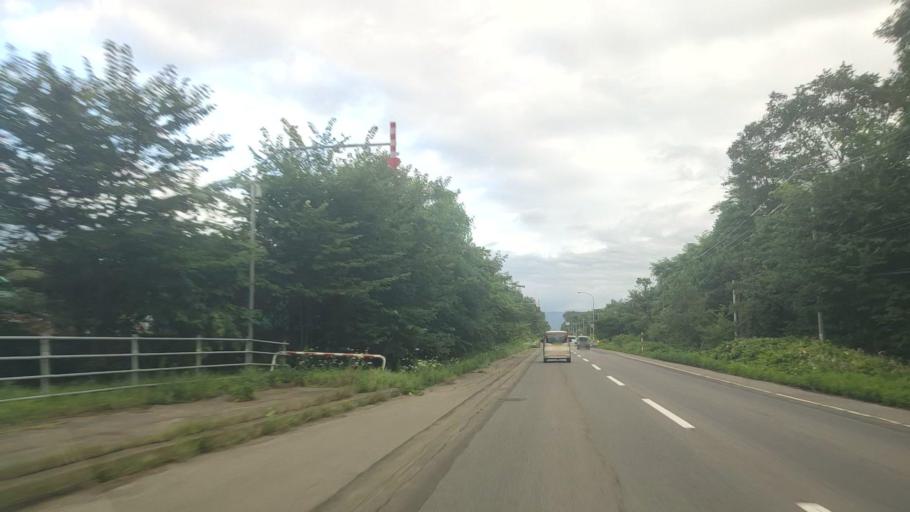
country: JP
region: Hokkaido
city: Nanae
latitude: 42.0219
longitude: 140.6158
